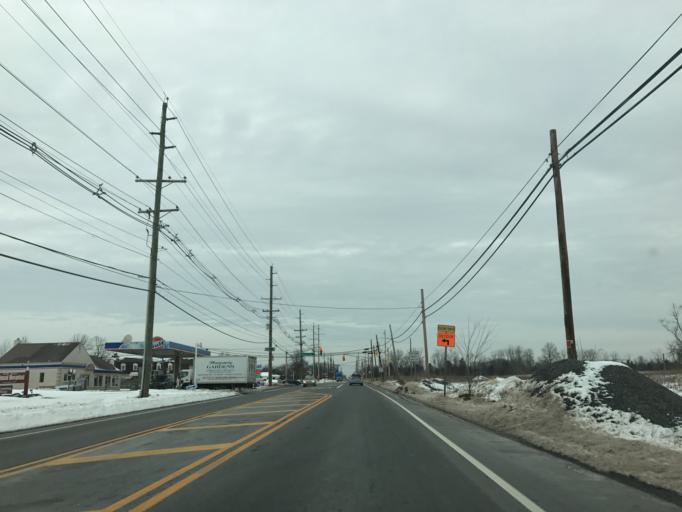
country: US
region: New Jersey
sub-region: Somerset County
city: Bloomingdale
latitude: 40.4770
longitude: -74.6558
